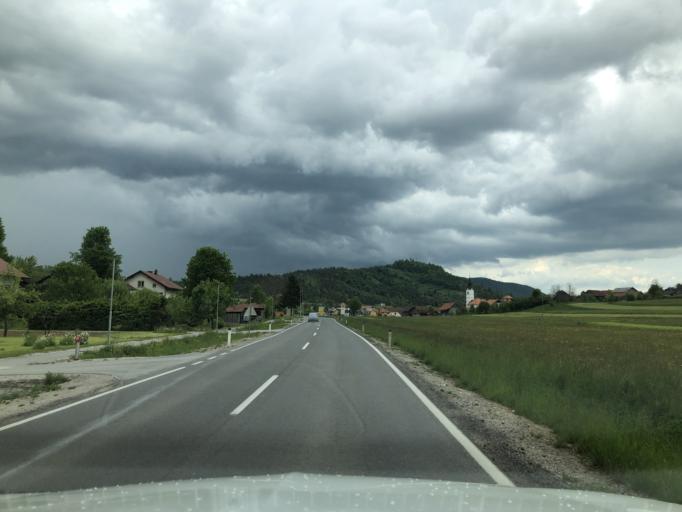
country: SI
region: Cerknica
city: Rakek
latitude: 45.8175
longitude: 14.2964
